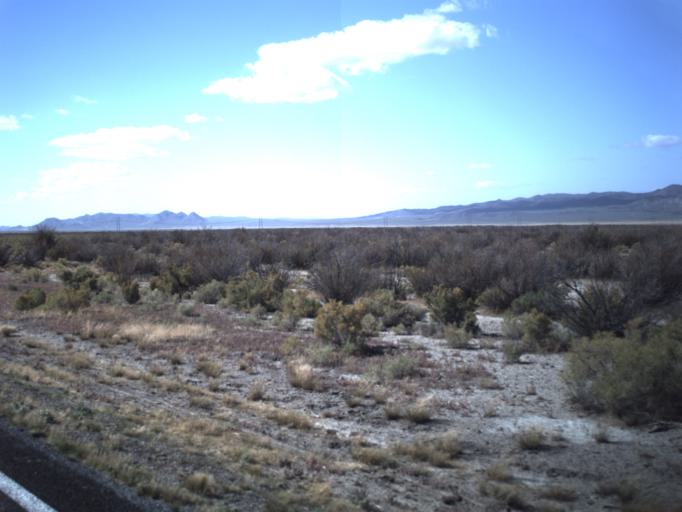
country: US
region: Utah
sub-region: Beaver County
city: Milford
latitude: 38.5870
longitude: -112.9886
